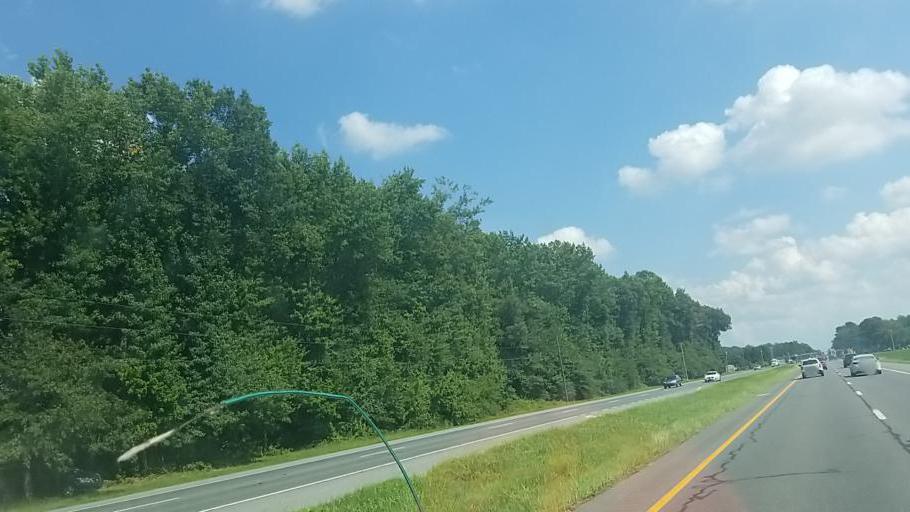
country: US
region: Delaware
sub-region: Sussex County
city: Georgetown
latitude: 38.6564
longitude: -75.3714
